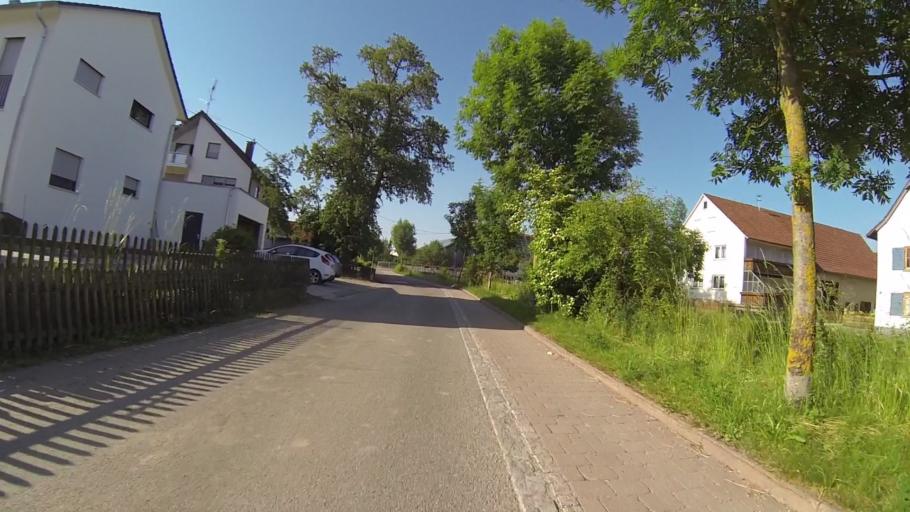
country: DE
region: Baden-Wuerttemberg
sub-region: Tuebingen Region
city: Mietingen
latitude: 48.1712
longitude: 9.8638
